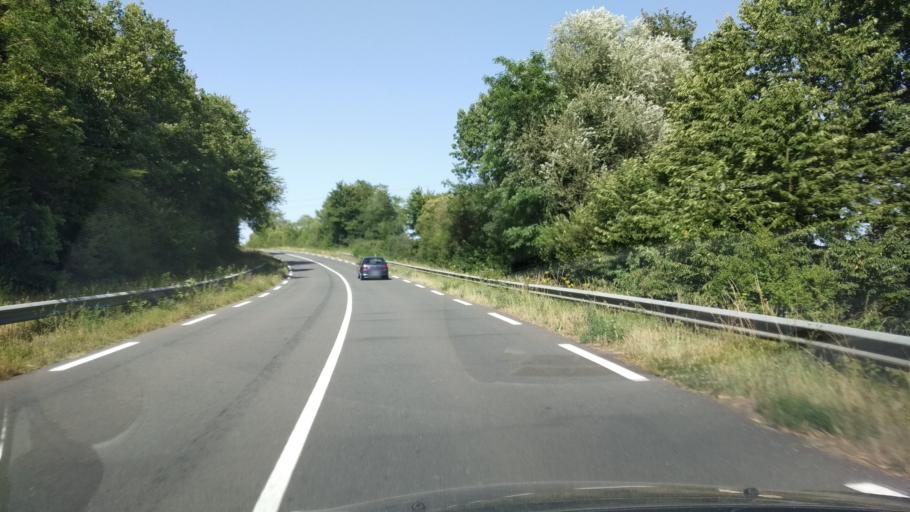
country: FR
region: Poitou-Charentes
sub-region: Departement de la Vienne
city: Lussac-les-Chateaux
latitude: 46.4241
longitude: 0.6361
